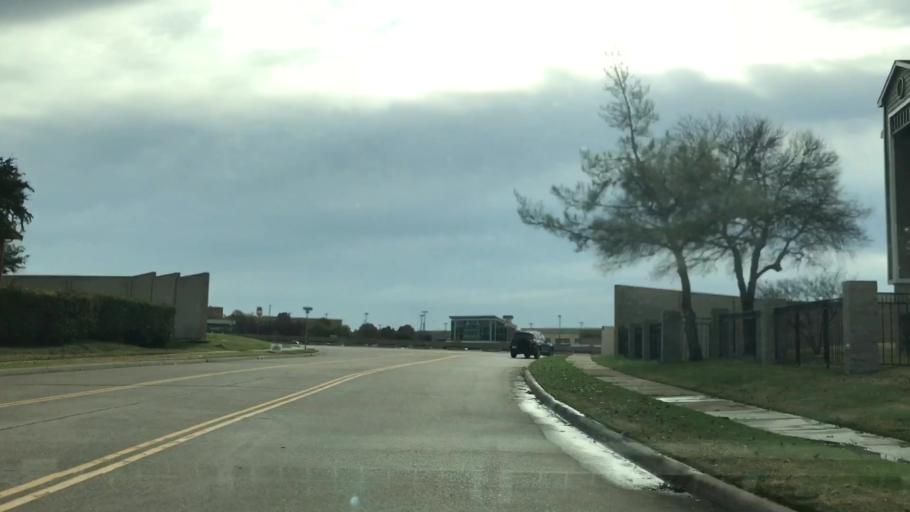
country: US
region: Texas
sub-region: Dallas County
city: Farmers Branch
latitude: 32.9034
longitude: -96.9624
